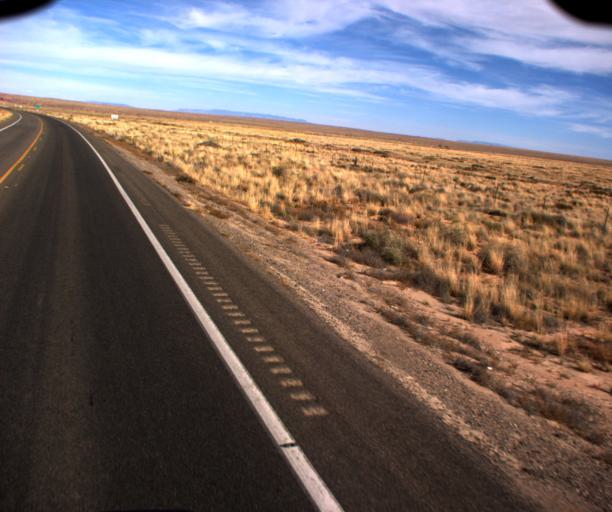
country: US
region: Arizona
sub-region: Navajo County
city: Kayenta
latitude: 36.7297
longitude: -110.1057
